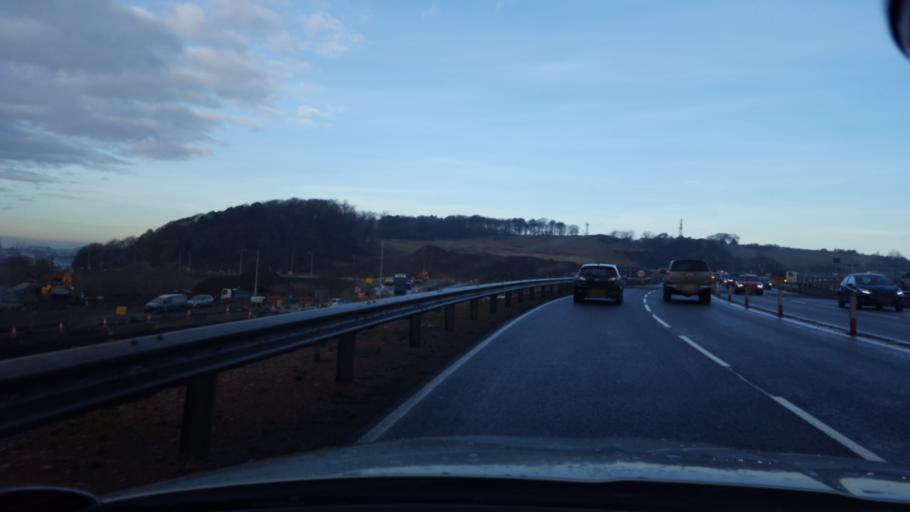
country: GB
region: Scotland
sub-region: Fife
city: Inverkeithing
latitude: 56.0195
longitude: -3.4060
